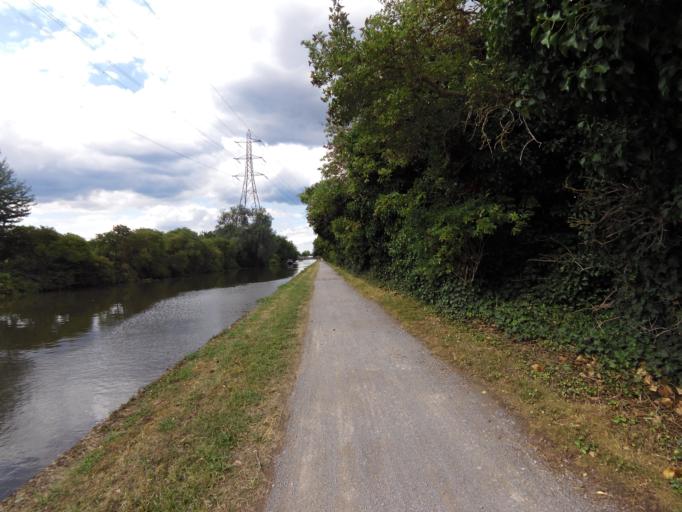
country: GB
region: England
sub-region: Greater London
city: Walthamstow
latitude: 51.6352
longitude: -0.0306
